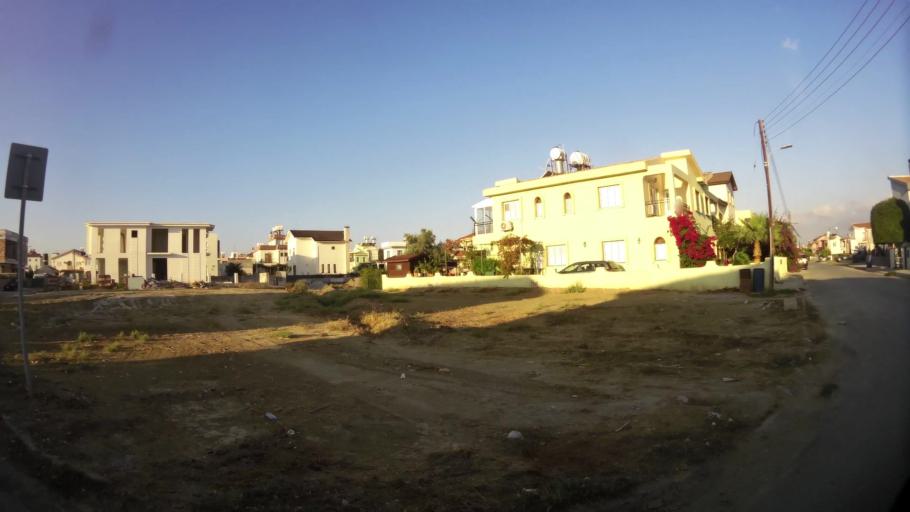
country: CY
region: Lefkosia
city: Nicosia
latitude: 35.1950
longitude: 33.3246
